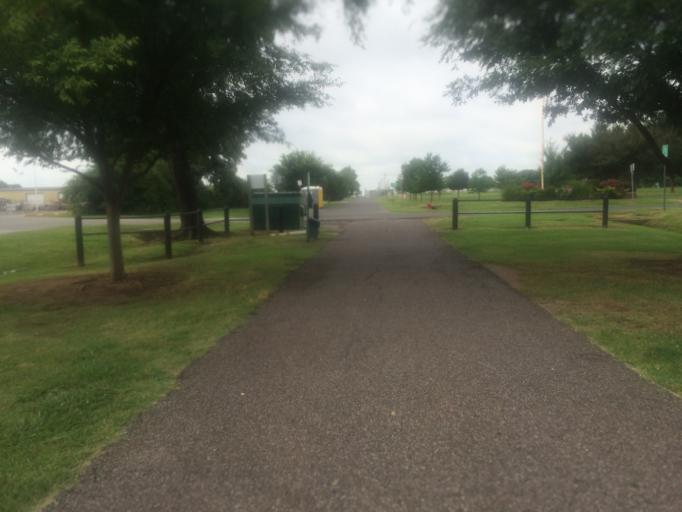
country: US
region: Oklahoma
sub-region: Cleveland County
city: Norman
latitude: 35.1939
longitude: -97.4396
